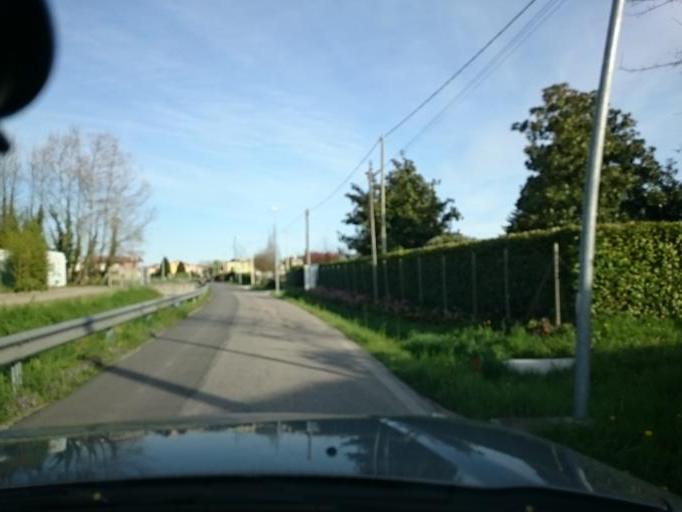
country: IT
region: Veneto
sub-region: Provincia di Padova
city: Mandriola-Sant'Agostino
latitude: 45.3679
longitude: 11.8618
